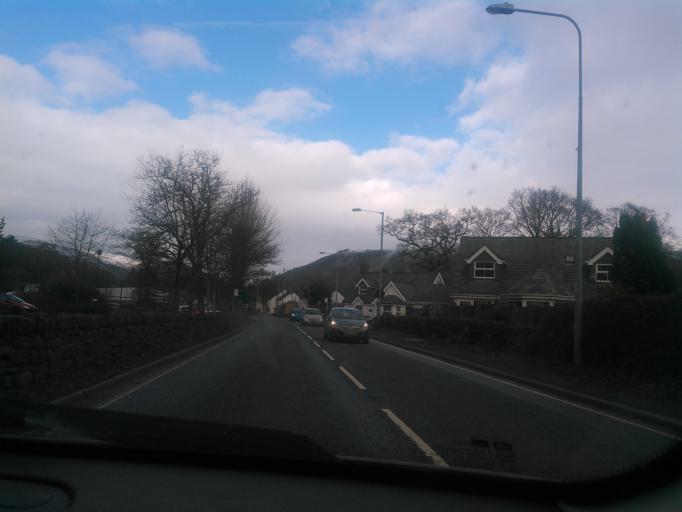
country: GB
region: Wales
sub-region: Denbighshire
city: Llangollen
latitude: 52.9737
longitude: -3.1800
